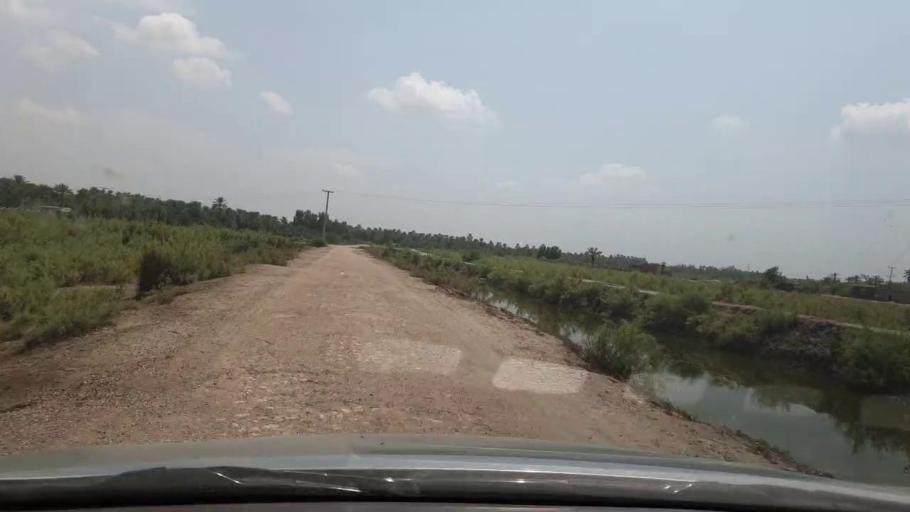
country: PK
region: Sindh
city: Kot Diji
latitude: 27.3774
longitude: 68.7107
